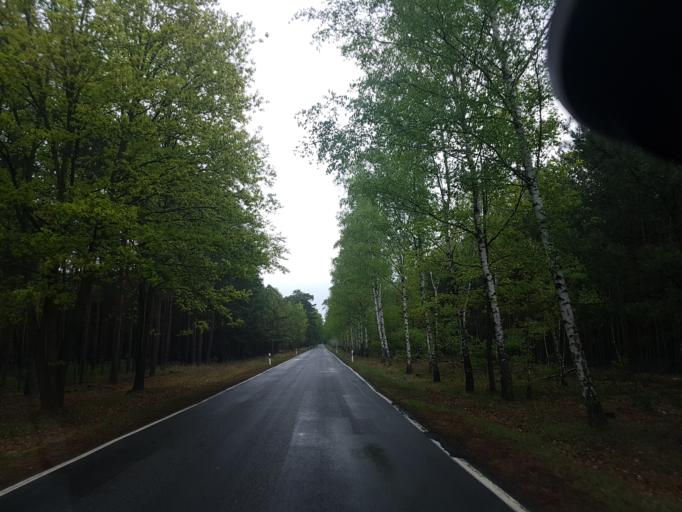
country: DE
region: Brandenburg
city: Spremberg
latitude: 51.6211
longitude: 14.4172
